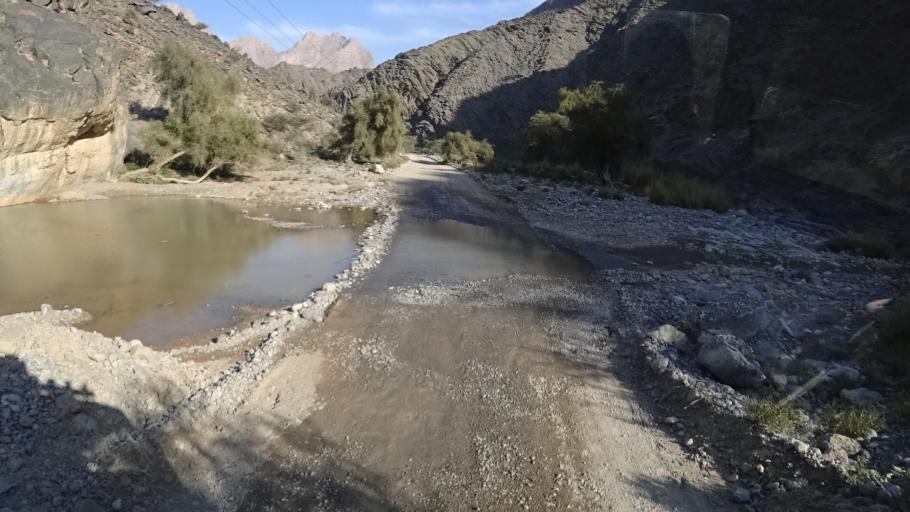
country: OM
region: Al Batinah
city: Bayt al `Awabi
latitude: 23.2246
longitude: 57.4157
